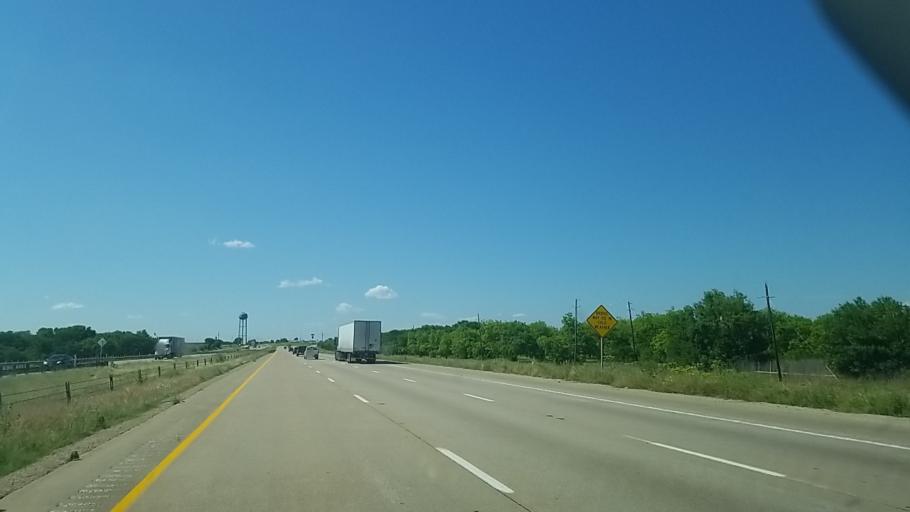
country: US
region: Texas
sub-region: Ellis County
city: Palmer
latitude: 32.4054
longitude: -96.6570
